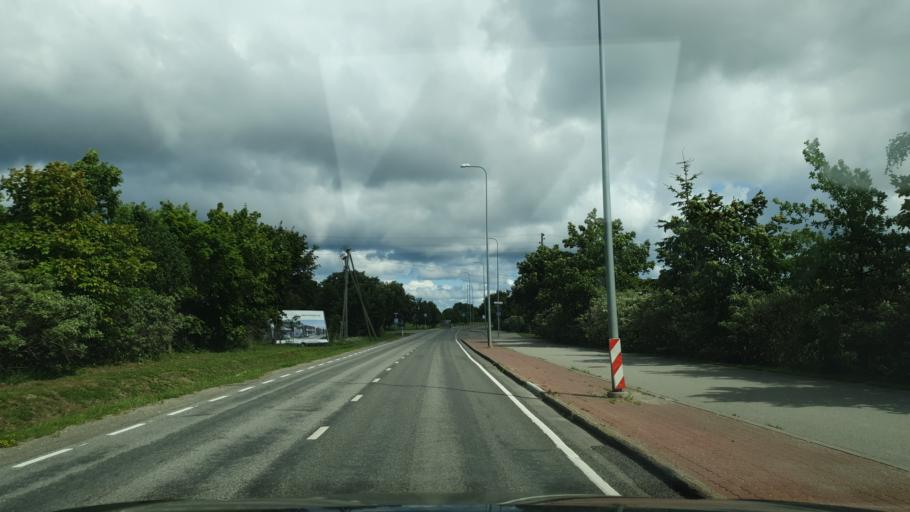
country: EE
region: Harju
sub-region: Viimsi vald
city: Viimsi
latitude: 59.5070
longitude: 24.8482
